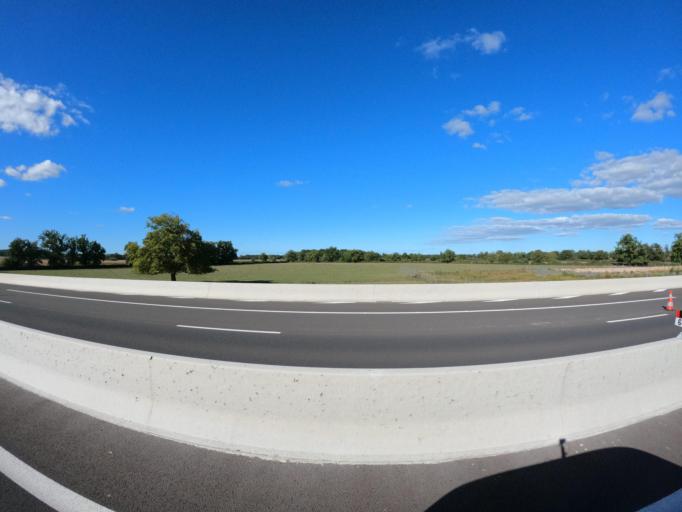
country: FR
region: Auvergne
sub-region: Departement de l'Allier
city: Dompierre-sur-Besbre
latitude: 46.5399
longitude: 3.6838
